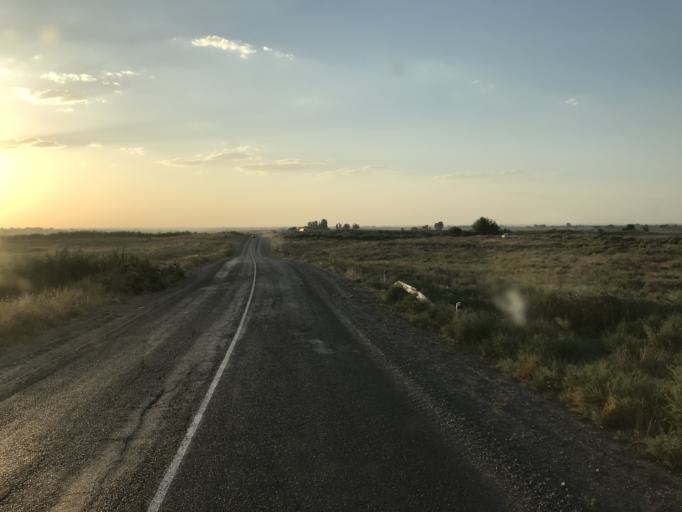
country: UZ
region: Toshkent
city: Yangiyul
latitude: 41.3422
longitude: 68.8777
